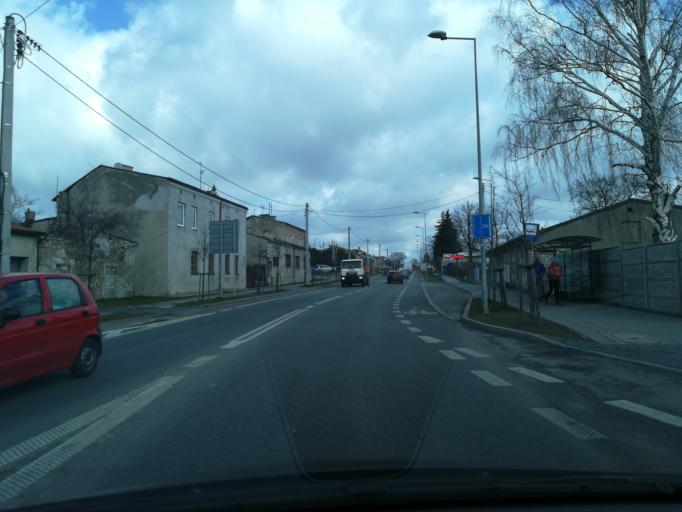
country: PL
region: Silesian Voivodeship
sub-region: Czestochowa
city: Czestochowa
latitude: 50.8241
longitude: 19.1342
